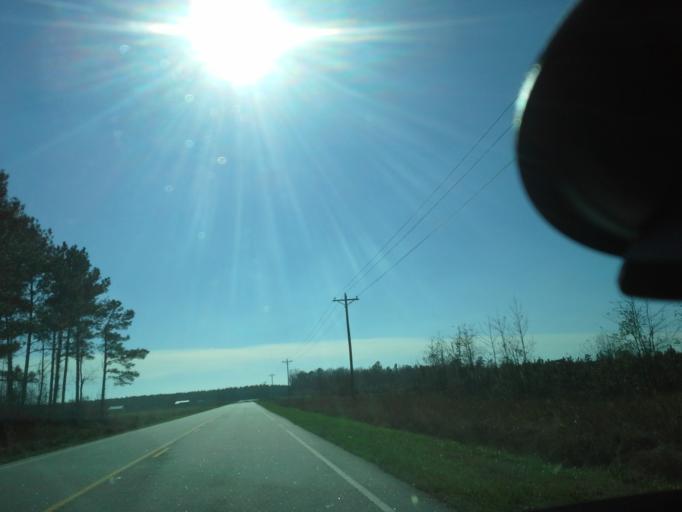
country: US
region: North Carolina
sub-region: Beaufort County
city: Belhaven
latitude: 35.5657
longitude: -76.6974
